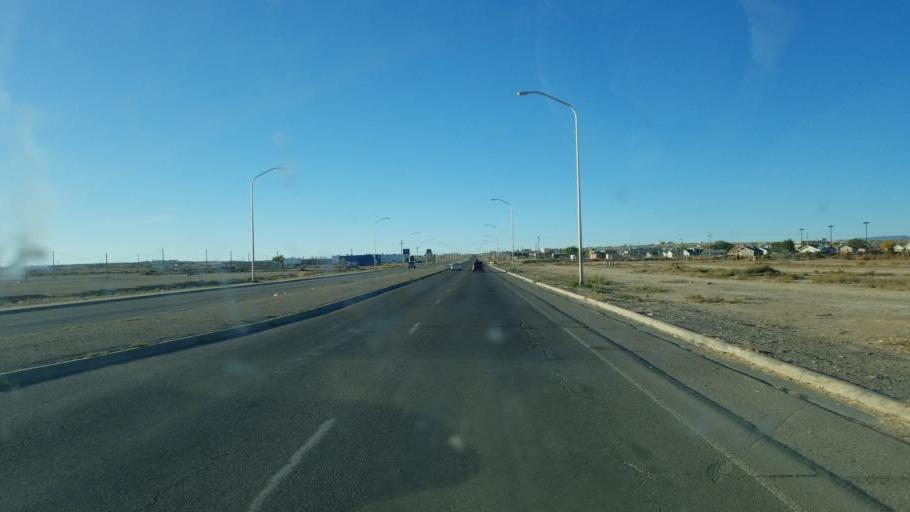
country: US
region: New Mexico
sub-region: San Juan County
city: Shiprock
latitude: 36.7724
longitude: -108.6978
